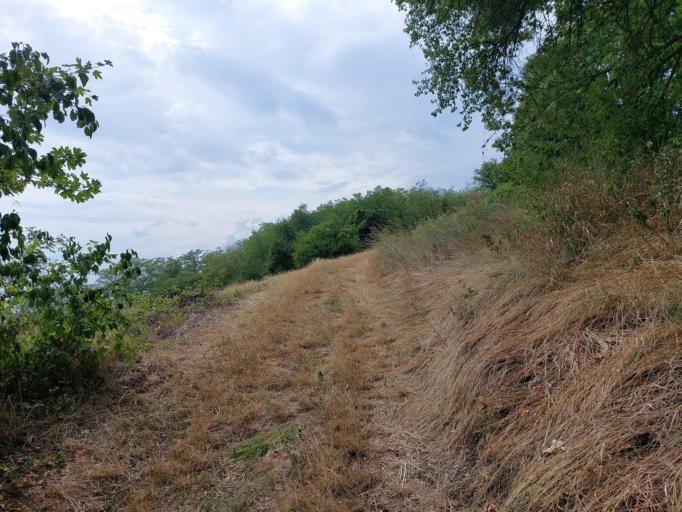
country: HU
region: Veszprem
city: Devecser
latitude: 47.1436
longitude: 17.3699
